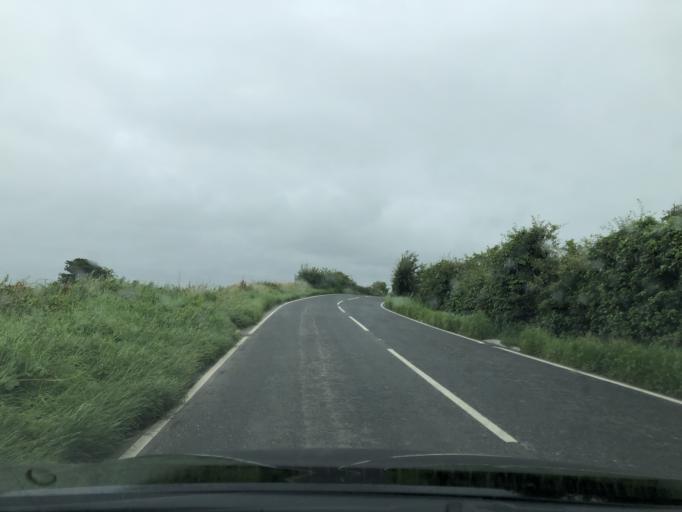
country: GB
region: Northern Ireland
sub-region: Down District
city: Dundrum
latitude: 54.2860
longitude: -5.8171
